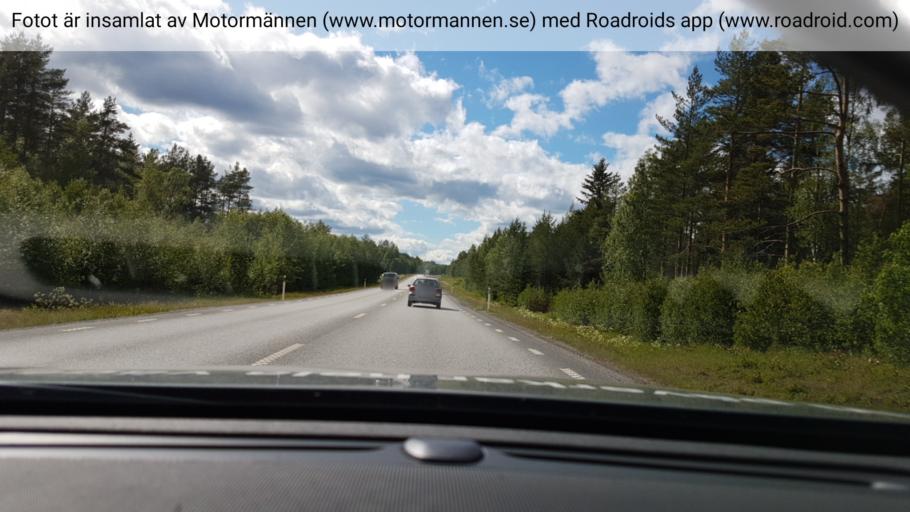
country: SE
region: Vaesterbotten
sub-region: Umea Kommun
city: Roback
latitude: 63.8469
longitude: 20.1476
